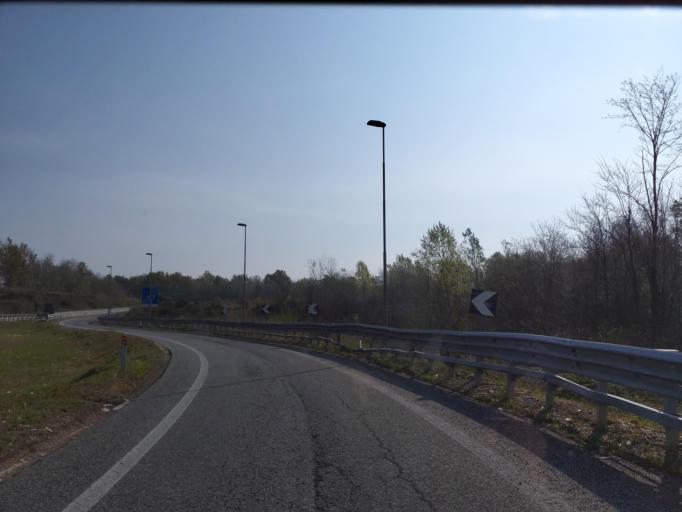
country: IT
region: Piedmont
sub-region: Provincia di Biella
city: Castelletto Cervo
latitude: 45.5517
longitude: 8.2384
